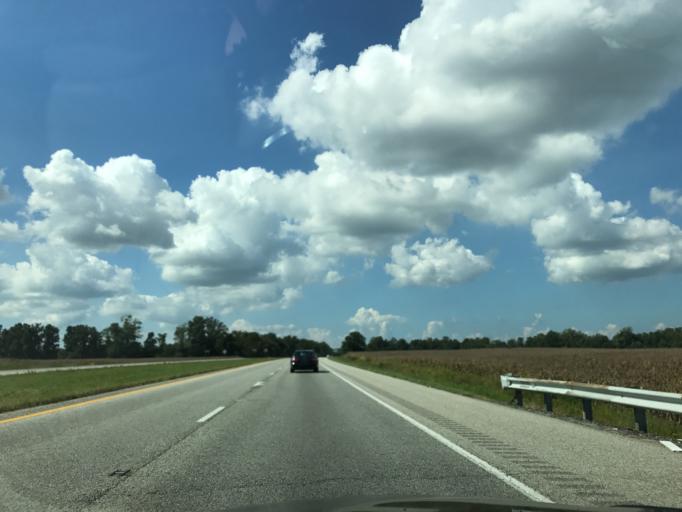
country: US
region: Maryland
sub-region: Queen Anne's County
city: Centreville
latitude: 39.0168
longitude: -76.0578
